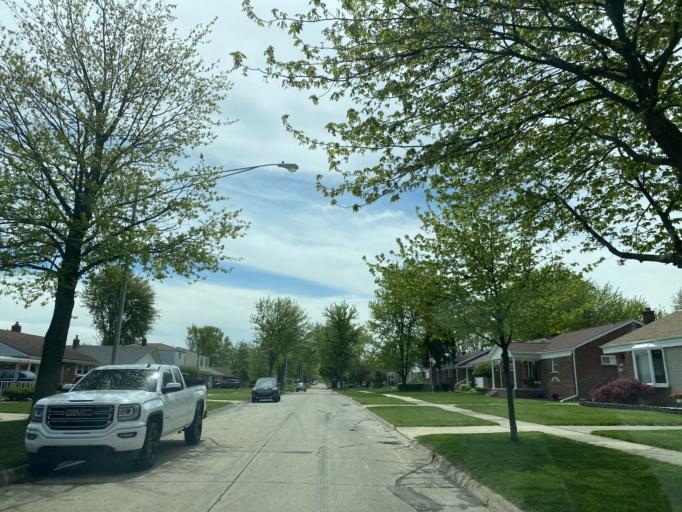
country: US
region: Michigan
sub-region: Wayne County
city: Riverview
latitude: 42.1753
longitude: -83.1862
